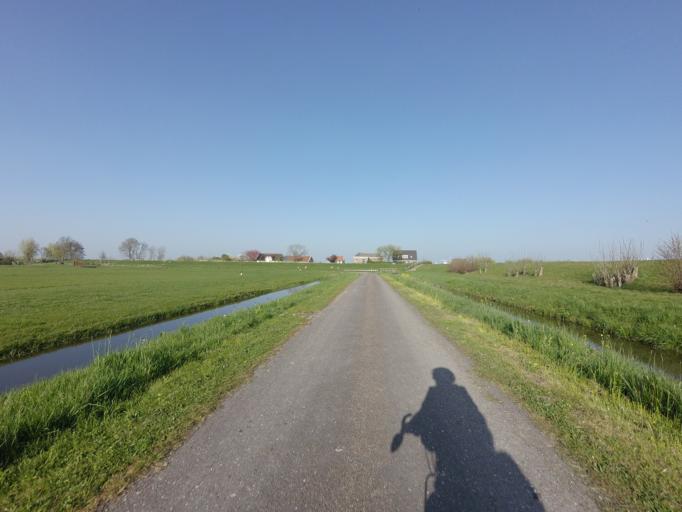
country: NL
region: South Holland
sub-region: Gemeente Vlaardingen
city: Vlaardingen
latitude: 51.9468
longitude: 4.3191
